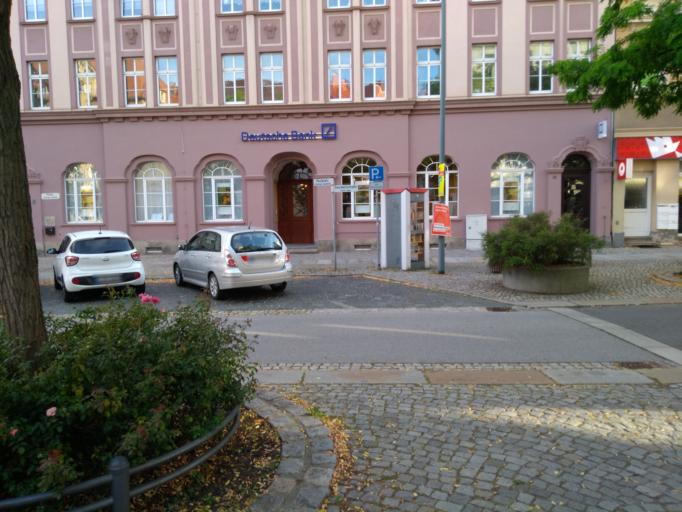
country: DE
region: Saxony
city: Bautzen
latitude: 51.1781
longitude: 14.4282
